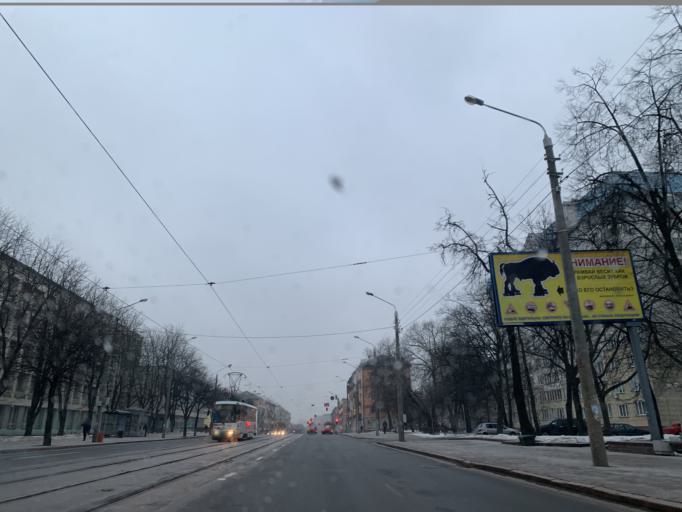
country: BY
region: Minsk
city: Minsk
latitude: 53.9214
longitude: 27.5888
